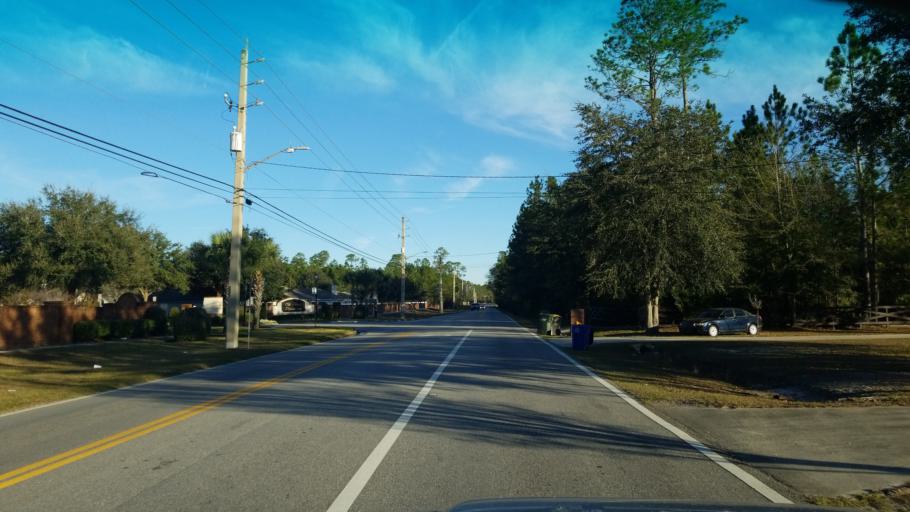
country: US
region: Florida
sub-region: Duval County
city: Baldwin
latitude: 30.3278
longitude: -81.8486
